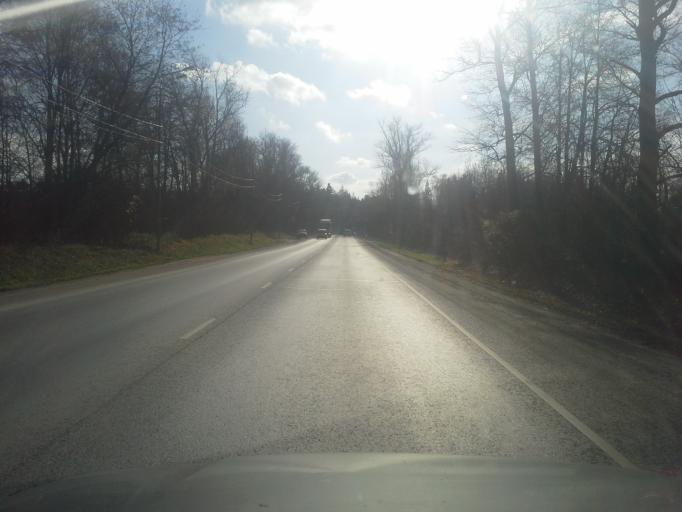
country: RU
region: Moskovskaya
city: Bol'shiye Vyazemy
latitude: 55.6617
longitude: 36.9659
